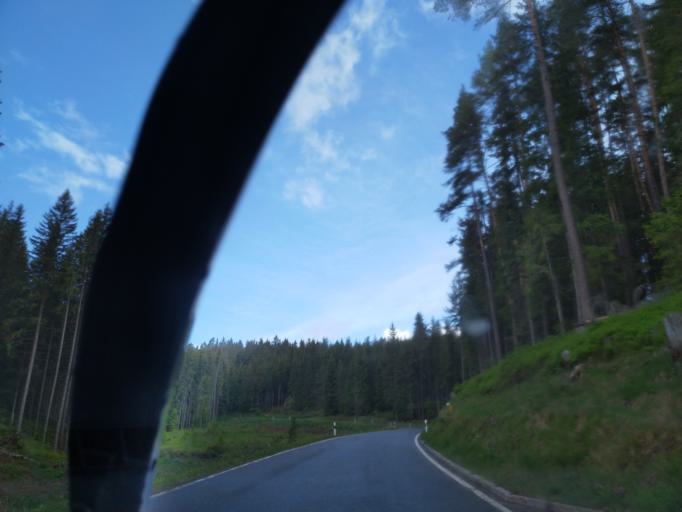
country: DE
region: Baden-Wuerttemberg
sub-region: Freiburg Region
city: Friedenweiler
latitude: 47.9315
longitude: 8.2584
